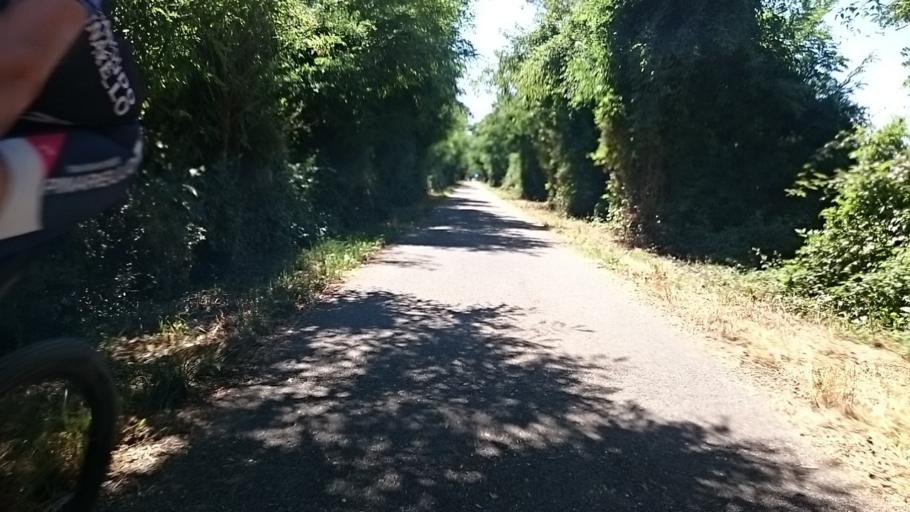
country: IT
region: Veneto
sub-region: Provincia di Padova
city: Trebaseleghe
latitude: 45.6189
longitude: 12.0587
